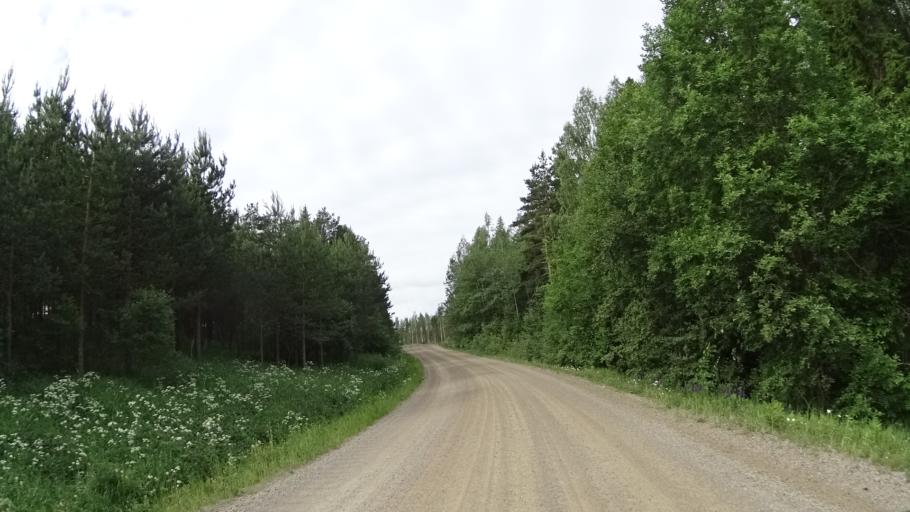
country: FI
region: Uusimaa
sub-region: Helsinki
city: Karkkila
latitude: 60.4739
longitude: 24.2555
